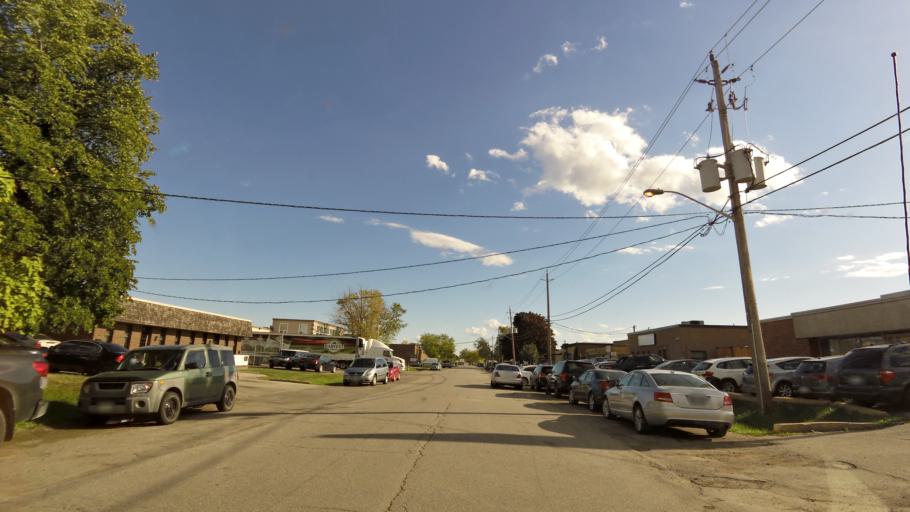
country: CA
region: Ontario
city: Etobicoke
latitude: 43.6045
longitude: -79.5282
